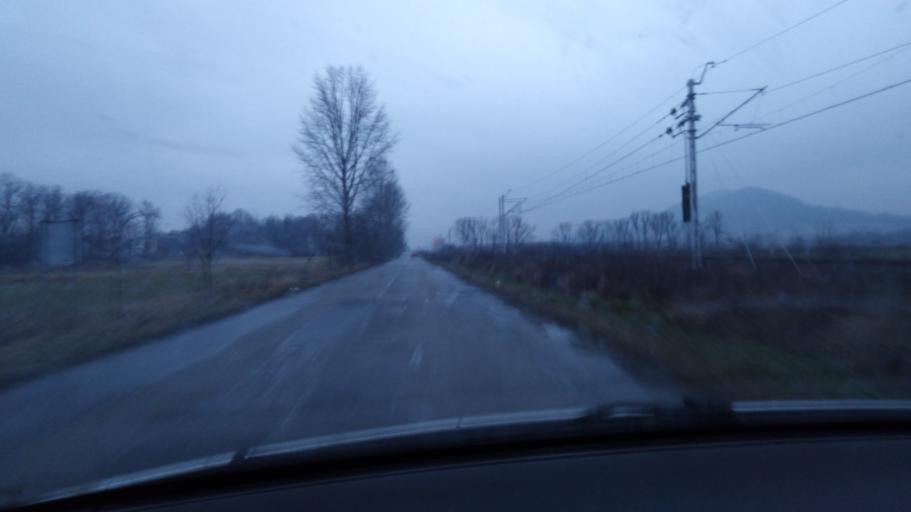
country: PL
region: Silesian Voivodeship
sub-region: Powiat zywiecki
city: Wieprz
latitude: 49.6408
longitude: 19.1588
